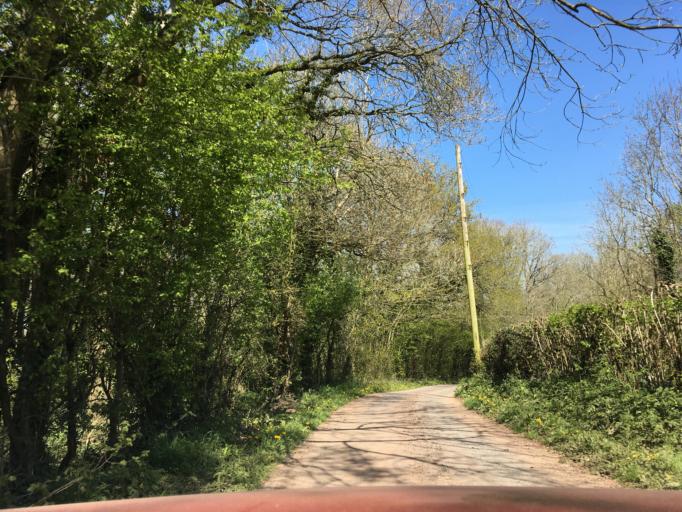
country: GB
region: Wales
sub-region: Monmouthshire
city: Llangwm
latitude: 51.7529
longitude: -2.8291
